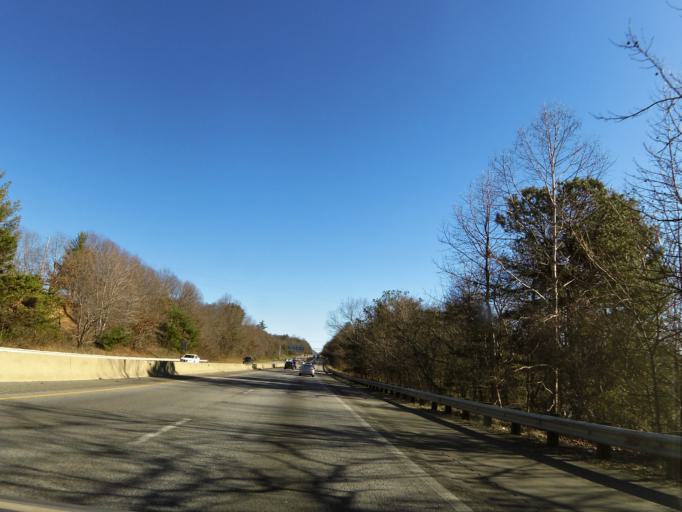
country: US
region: North Carolina
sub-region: Haywood County
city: Clyde
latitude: 35.5477
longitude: -82.8918
